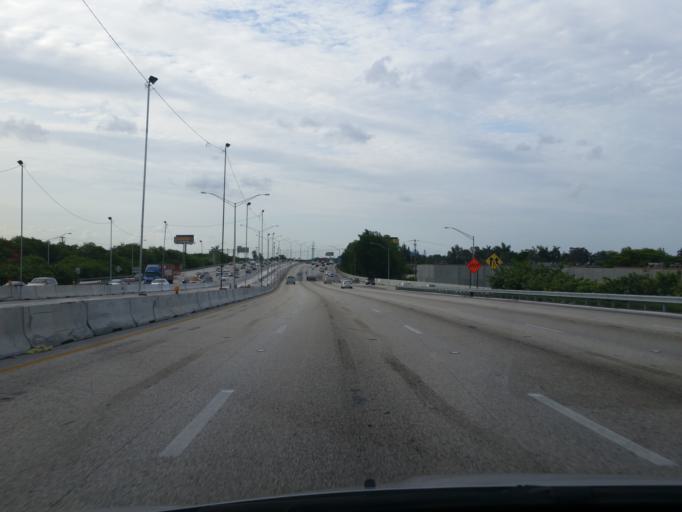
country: US
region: Florida
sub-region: Broward County
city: Hollywood
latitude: 26.0128
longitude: -80.1667
